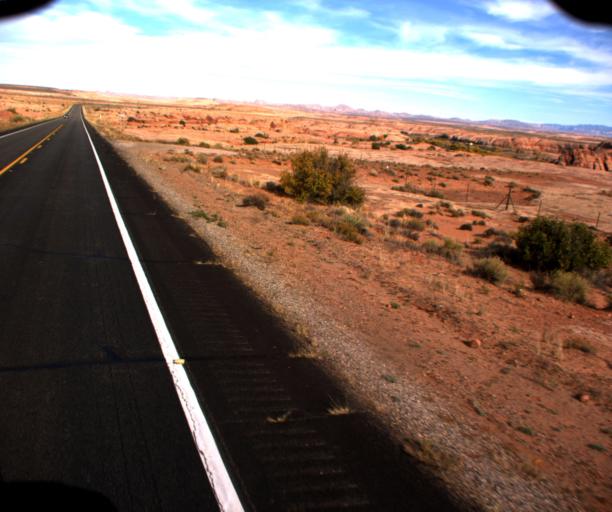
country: US
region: Arizona
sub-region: Navajo County
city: Kayenta
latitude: 36.9417
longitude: -109.7303
